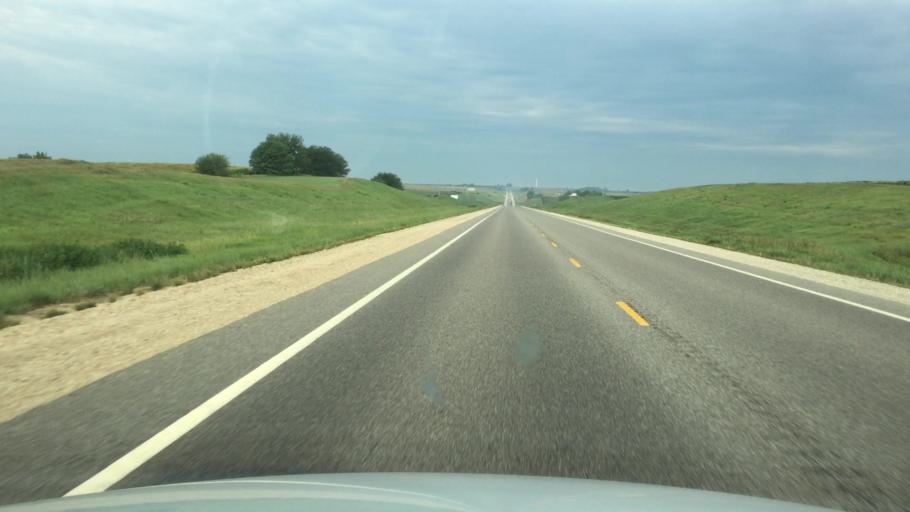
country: US
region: Kansas
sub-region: Doniphan County
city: Highland
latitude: 39.8422
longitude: -95.2958
